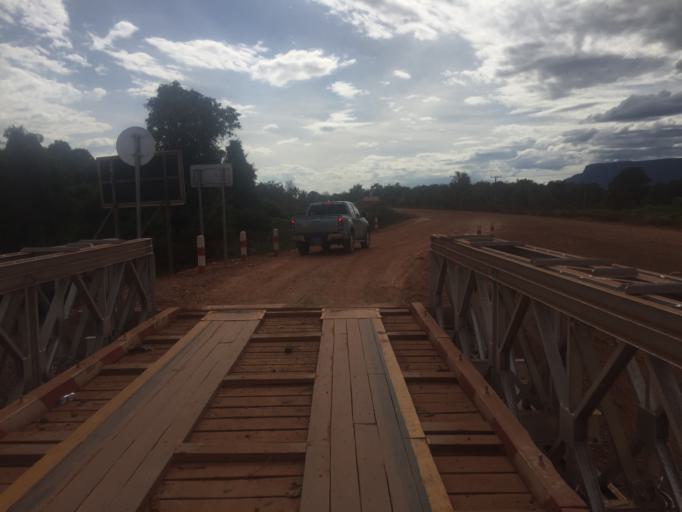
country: LA
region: Attapu
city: Attapu
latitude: 14.7504
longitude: 106.7018
